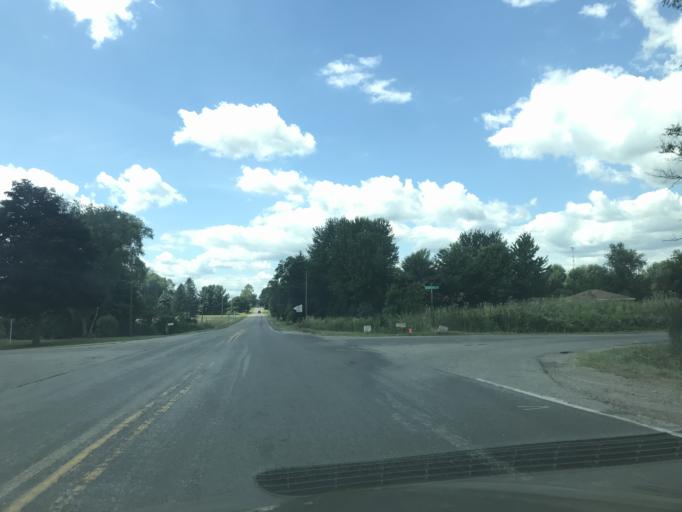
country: US
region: Michigan
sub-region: Ingham County
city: Leslie
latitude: 42.4512
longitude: -84.4470
